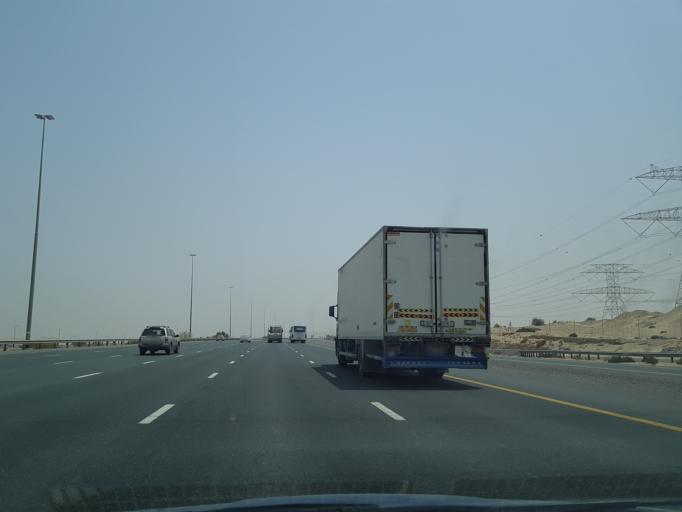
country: AE
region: Dubai
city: Dubai
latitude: 25.0583
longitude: 55.3201
